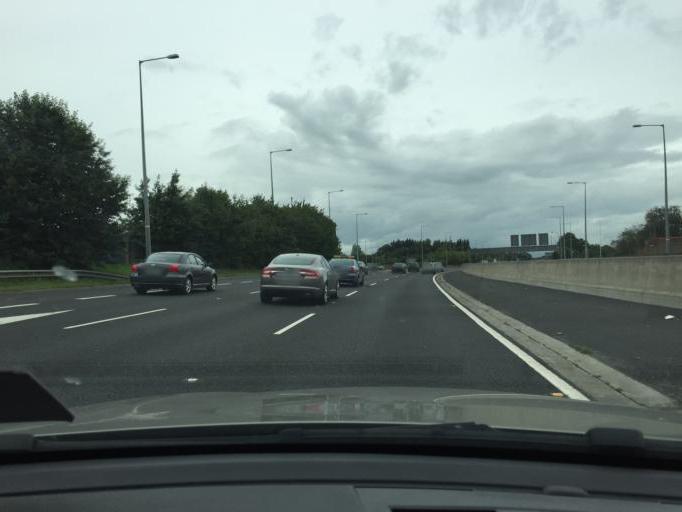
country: IE
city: Palmerstown
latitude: 53.3556
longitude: -6.3966
